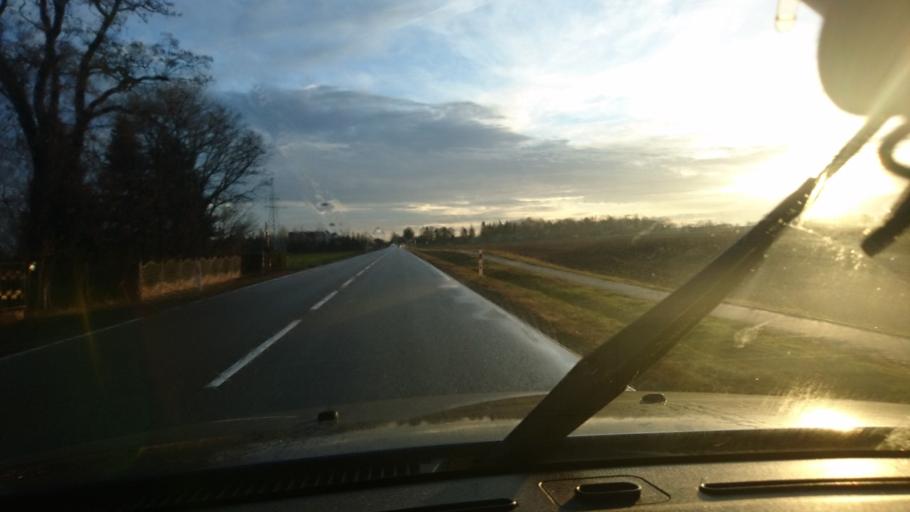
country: PL
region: Greater Poland Voivodeship
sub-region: Powiat kepinski
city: Opatow
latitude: 51.1876
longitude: 18.1471
